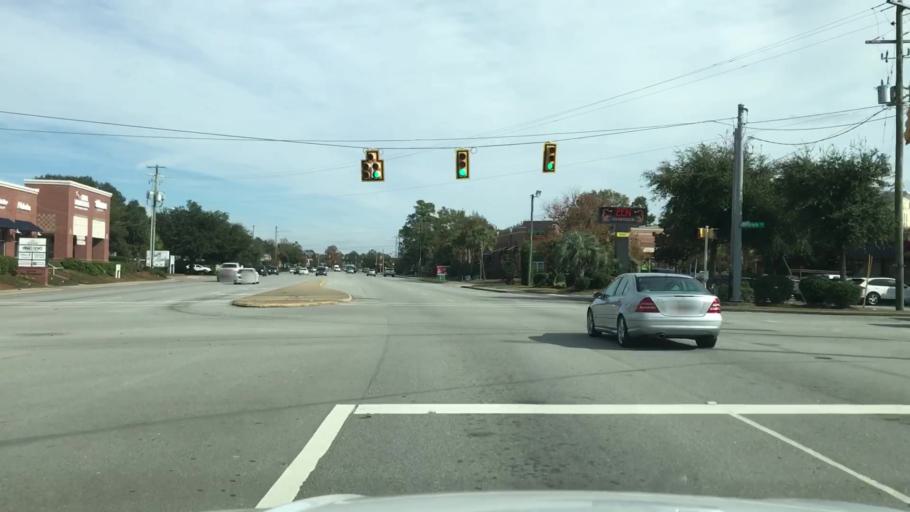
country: US
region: South Carolina
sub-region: Charleston County
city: Shell Point
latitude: 32.7923
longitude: -80.0304
